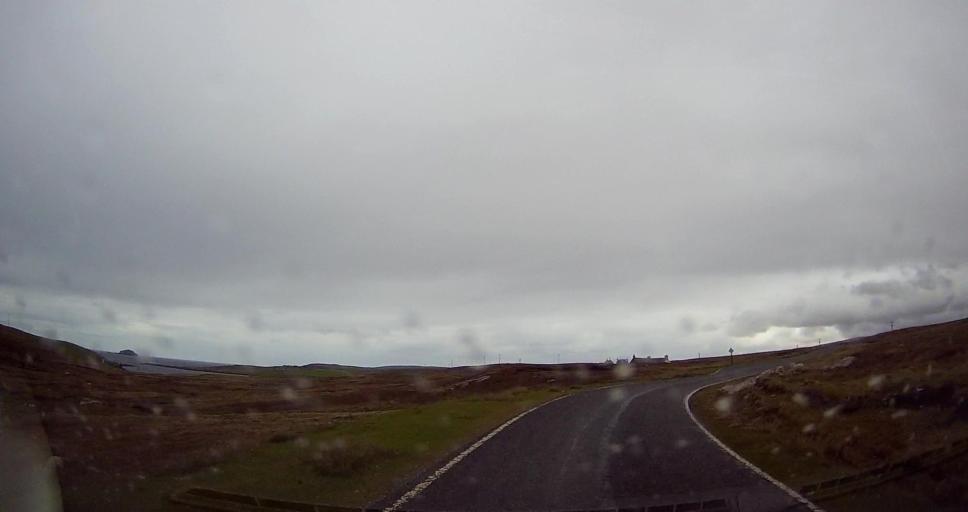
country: GB
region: Scotland
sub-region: Shetland Islands
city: Lerwick
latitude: 60.4928
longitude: -1.5707
